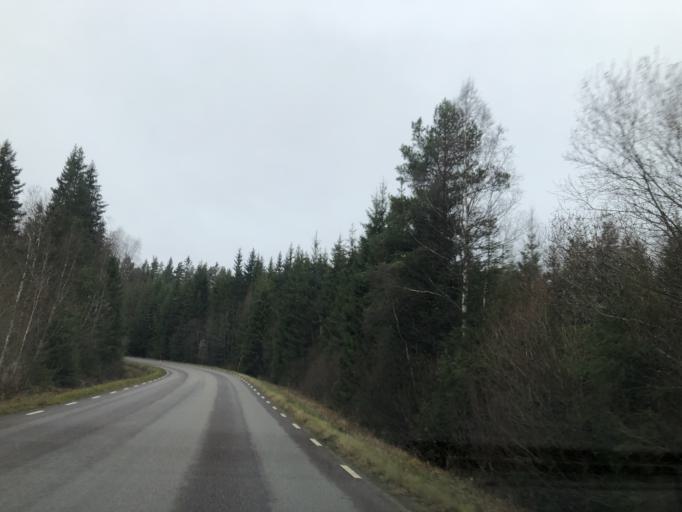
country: SE
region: Vaestra Goetaland
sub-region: Ulricehamns Kommun
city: Ulricehamn
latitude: 57.7693
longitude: 13.4539
